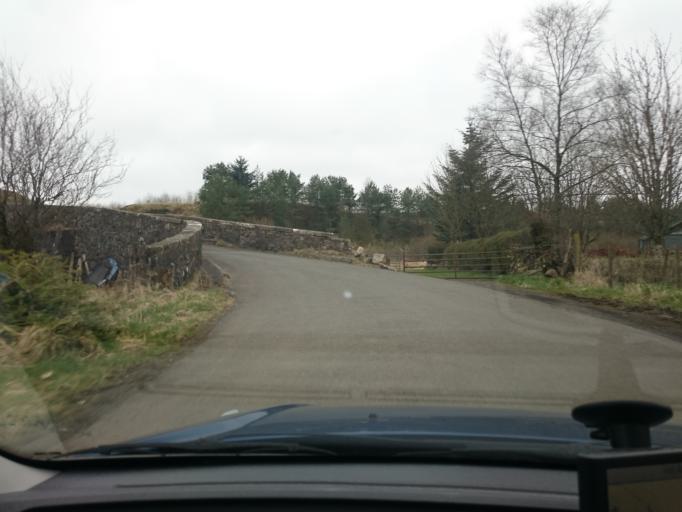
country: GB
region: Scotland
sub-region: North Lanarkshire
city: Kilsyth
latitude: 56.0283
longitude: -4.0215
